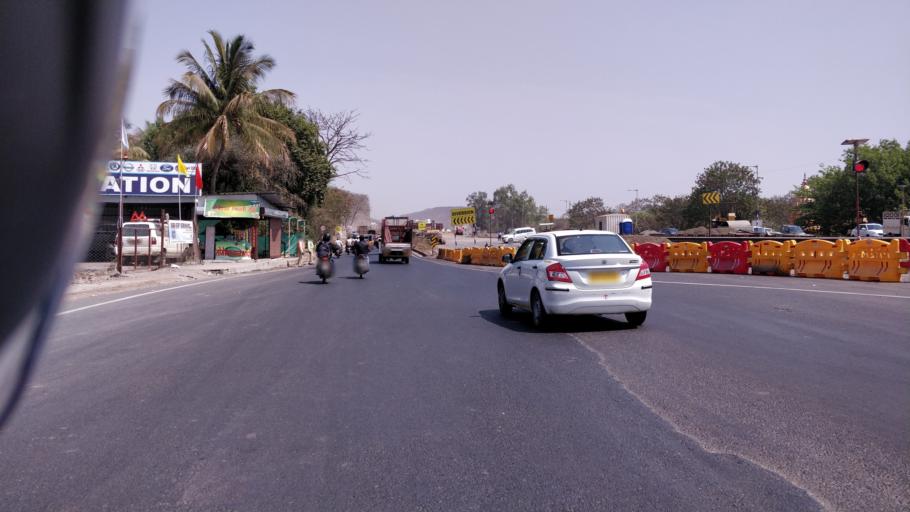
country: IN
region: Maharashtra
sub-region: Pune Division
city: Shivaji Nagar
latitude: 18.5318
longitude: 73.7795
